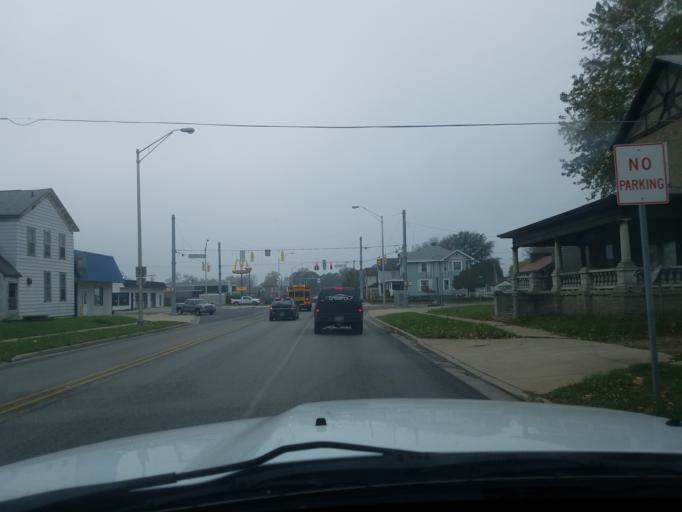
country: US
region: Indiana
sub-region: Cass County
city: Dunkirk
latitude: 40.7518
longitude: -86.3765
